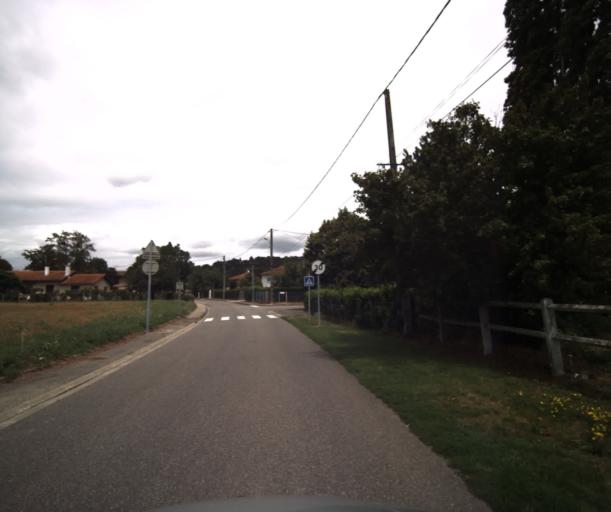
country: FR
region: Midi-Pyrenees
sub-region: Departement de la Haute-Garonne
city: Lacroix-Falgarde
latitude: 43.4889
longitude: 1.4071
